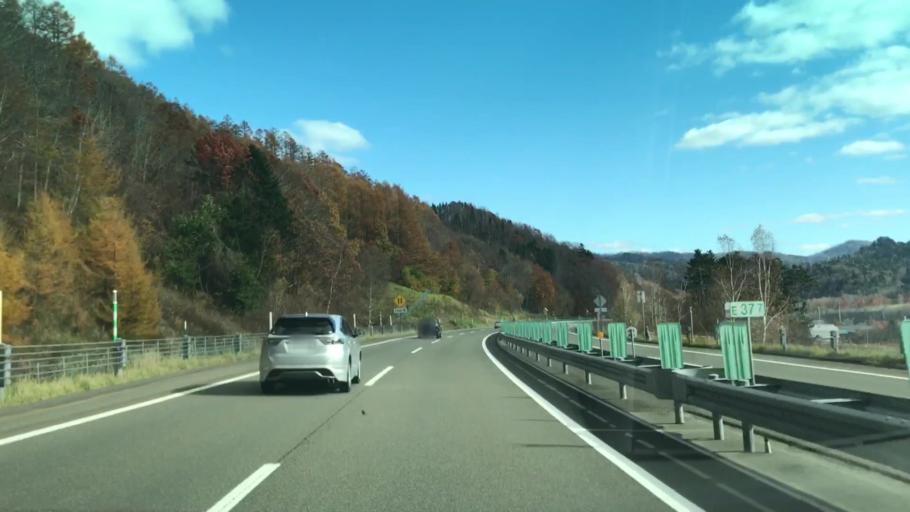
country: JP
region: Hokkaido
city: Chitose
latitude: 42.9080
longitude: 141.9944
